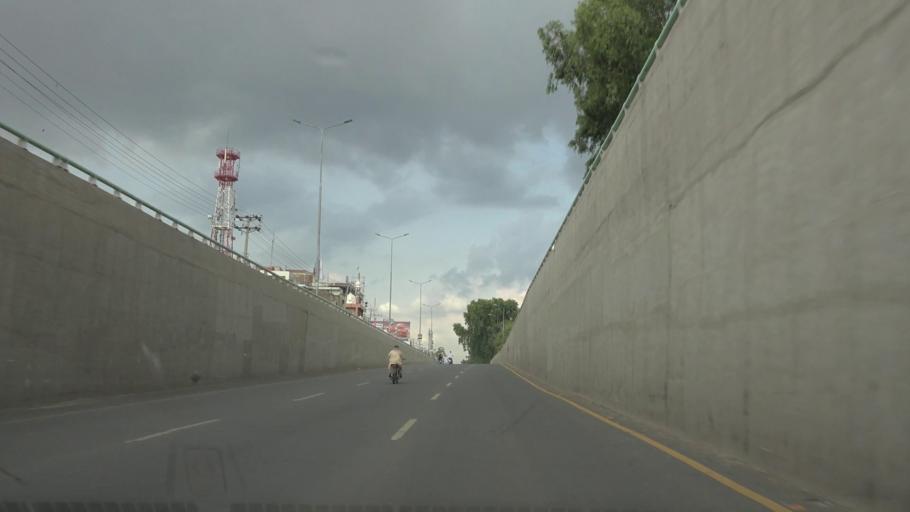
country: PK
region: Punjab
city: Faisalabad
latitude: 31.4263
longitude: 73.1148
